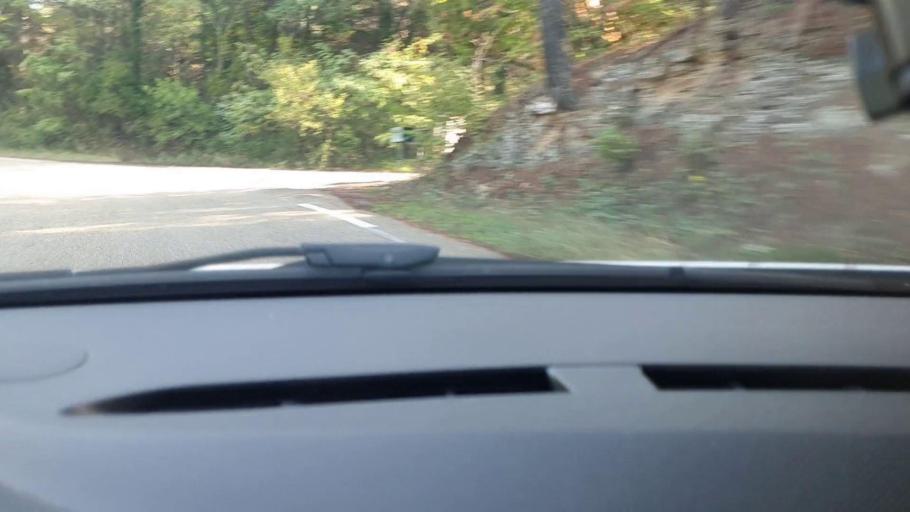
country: FR
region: Languedoc-Roussillon
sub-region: Departement du Gard
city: Molieres-sur-Ceze
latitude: 44.2518
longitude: 4.1354
